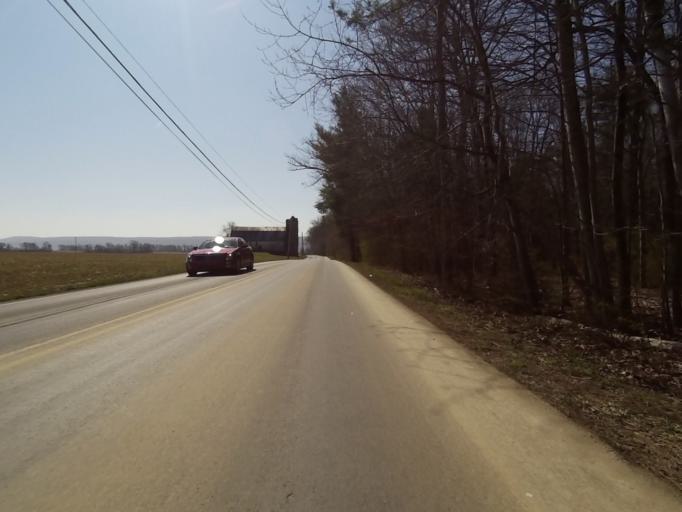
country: US
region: Pennsylvania
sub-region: Centre County
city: Park Forest Village
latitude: 40.7646
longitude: -77.9150
